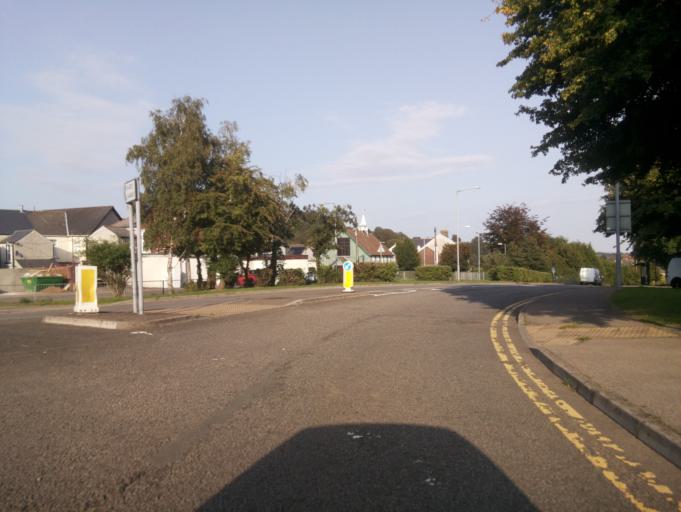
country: GB
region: Wales
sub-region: Torfaen County Borough
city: Pontypool
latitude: 51.6972
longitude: -3.0356
